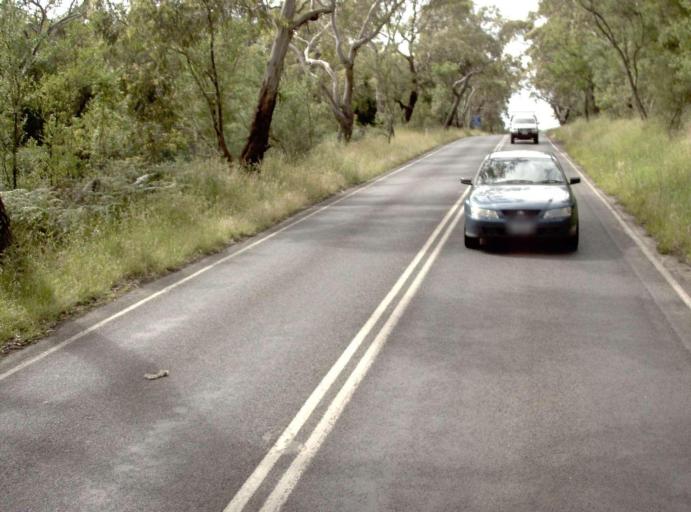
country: AU
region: Victoria
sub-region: Bass Coast
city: Phillip Island
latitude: -38.4848
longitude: 145.2603
